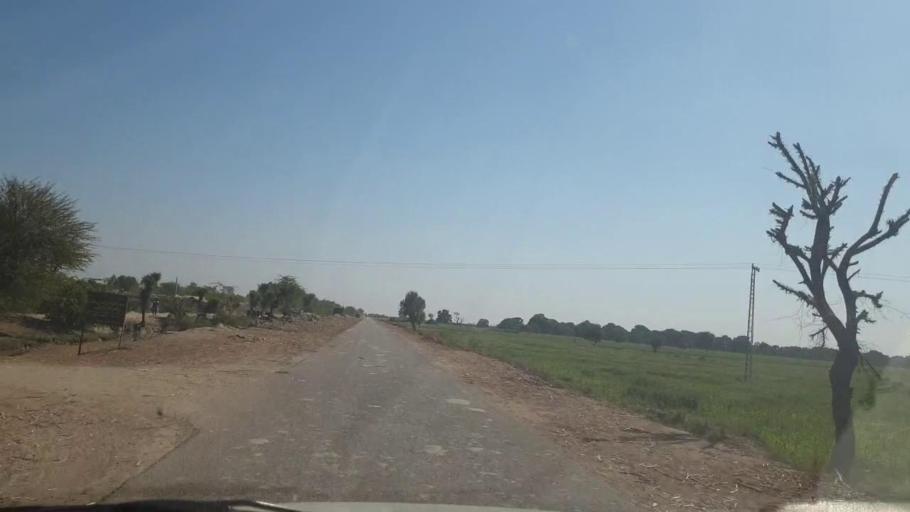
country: PK
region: Sindh
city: Mirpur Khas
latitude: 25.4652
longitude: 69.1790
